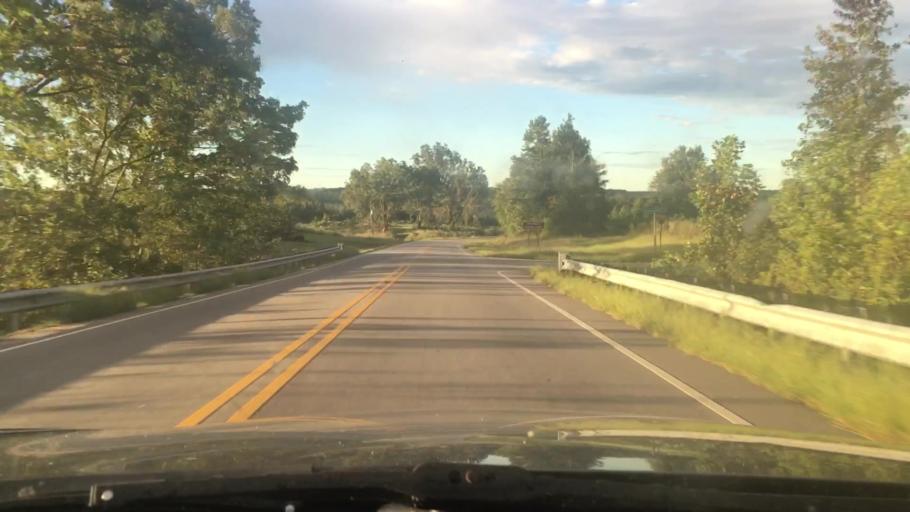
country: US
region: North Carolina
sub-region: Caswell County
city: Yanceyville
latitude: 36.3963
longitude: -79.3297
